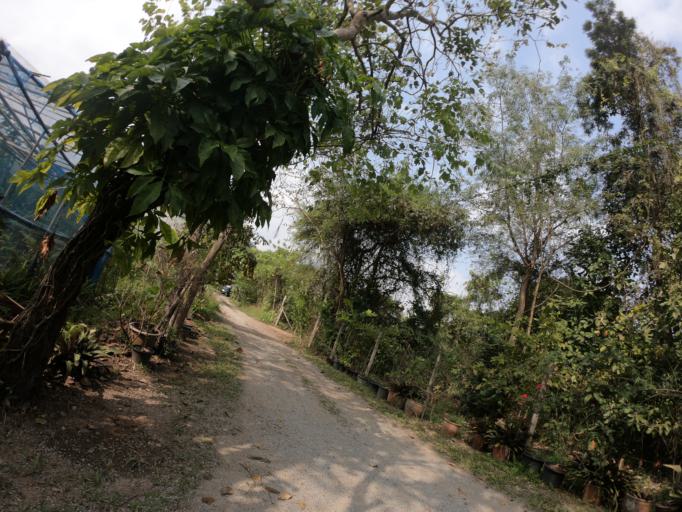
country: TH
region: Chiang Mai
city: Chiang Mai
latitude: 18.7557
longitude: 98.9778
